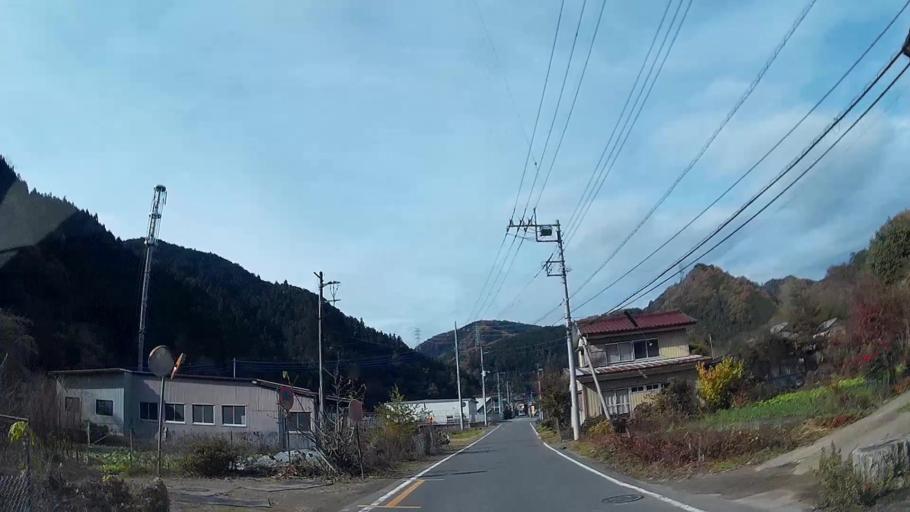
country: JP
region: Saitama
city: Chichibu
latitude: 36.0588
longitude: 138.9738
